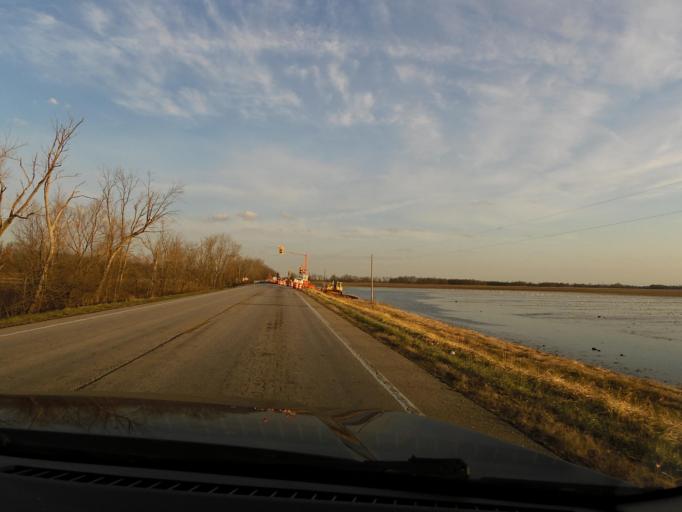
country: US
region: Illinois
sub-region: Fayette County
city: Vandalia
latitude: 38.9112
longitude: -89.0857
